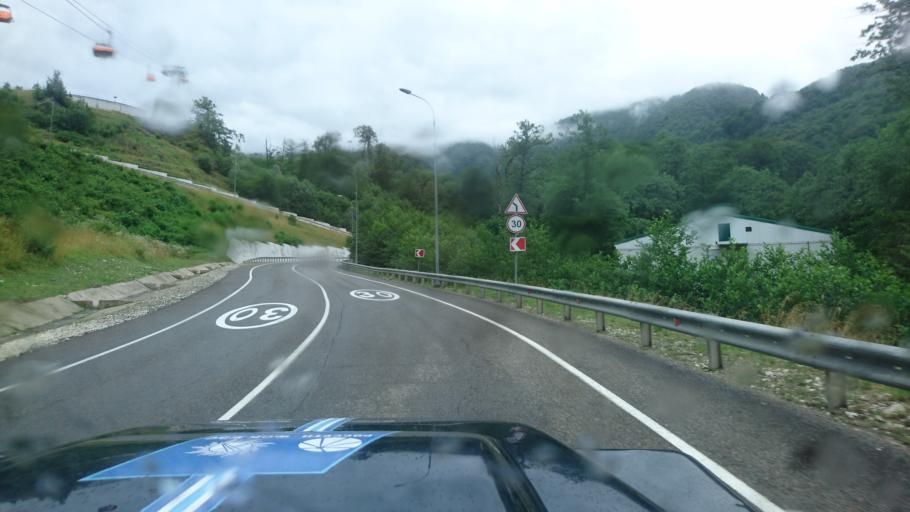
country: RU
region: Krasnodarskiy
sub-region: Sochi City
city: Krasnaya Polyana
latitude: 43.6733
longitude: 40.2857
